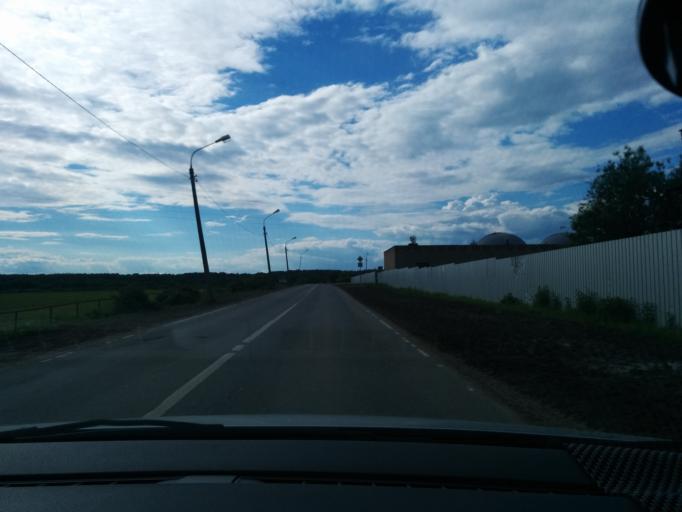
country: RU
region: Moskovskaya
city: Lugovaya
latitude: 56.0439
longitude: 37.4755
